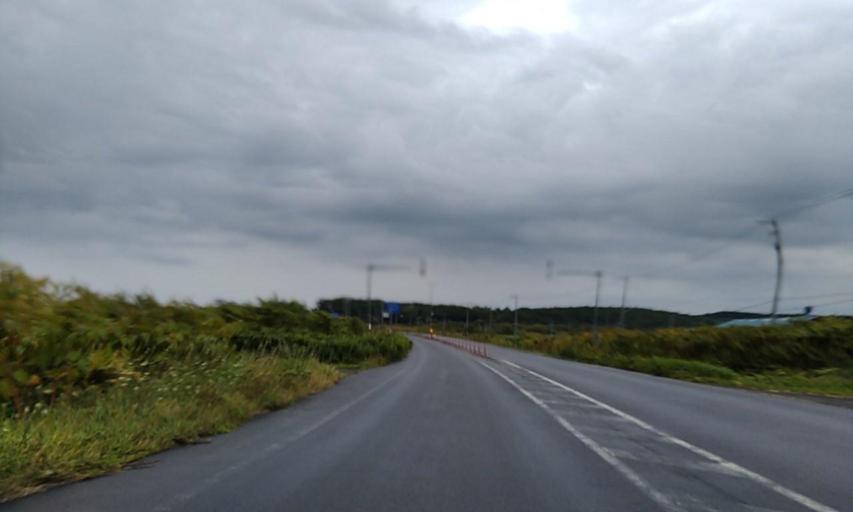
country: JP
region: Hokkaido
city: Nayoro
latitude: 44.6627
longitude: 142.8692
